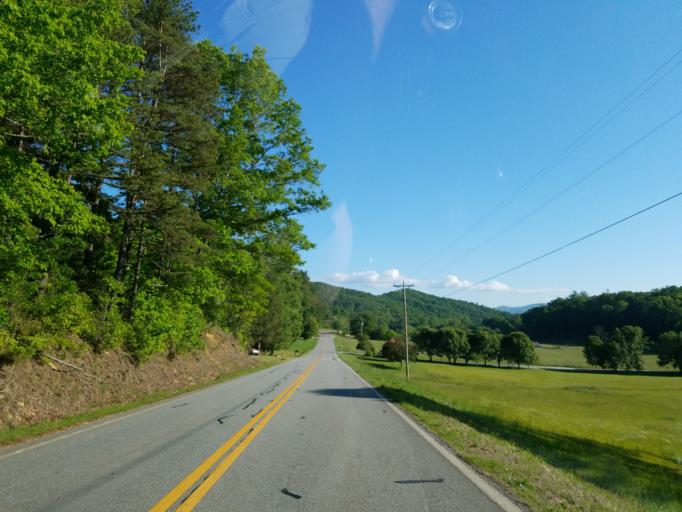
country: US
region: Georgia
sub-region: Fannin County
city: Blue Ridge
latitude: 34.7759
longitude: -84.1855
